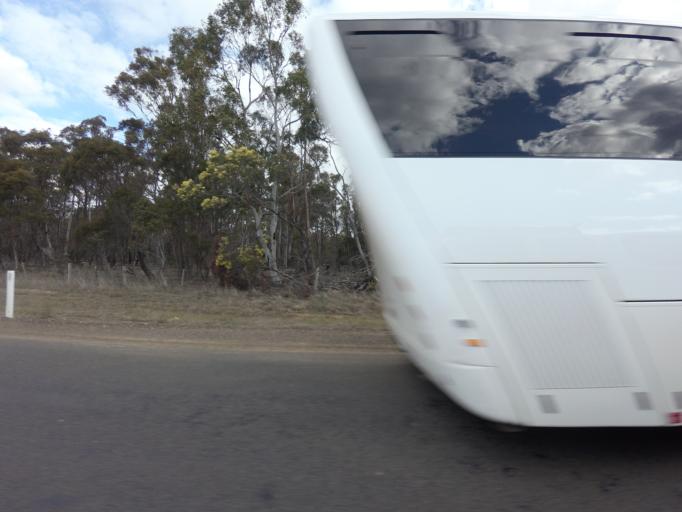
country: AU
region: Tasmania
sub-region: Northern Midlands
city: Longford
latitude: -41.8005
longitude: 147.1323
